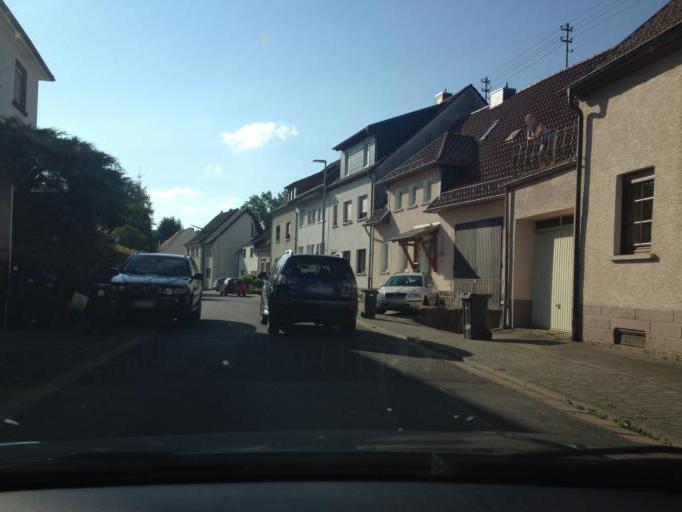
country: DE
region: Saarland
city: Ottweiler
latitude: 49.4309
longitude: 7.1675
